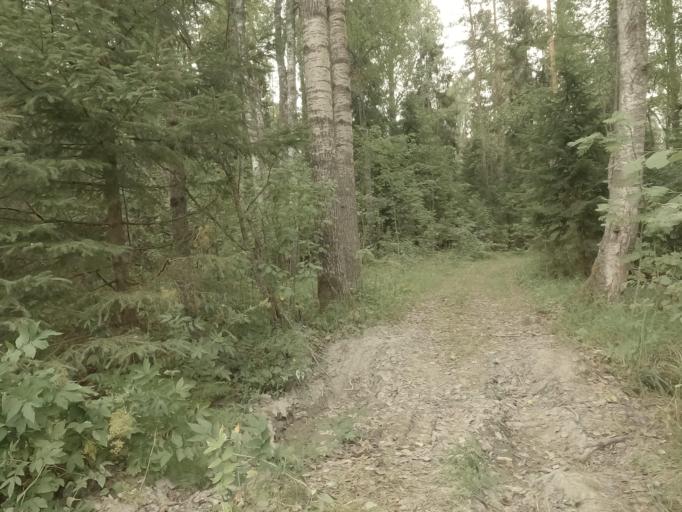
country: RU
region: Leningrad
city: Kamennogorsk
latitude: 61.0766
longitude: 29.1574
